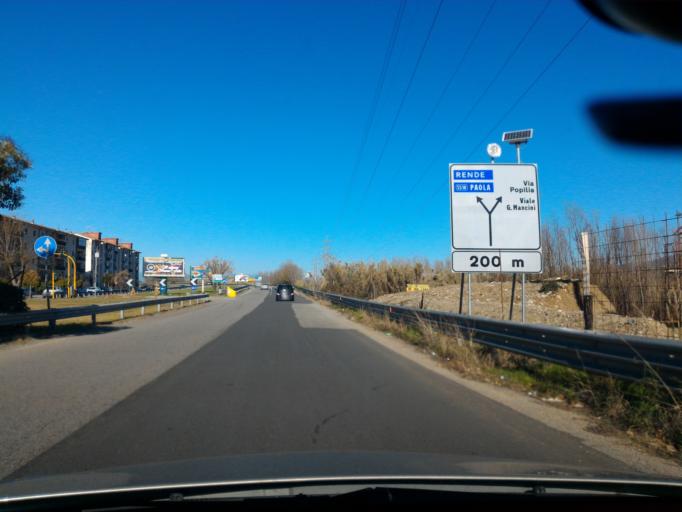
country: IT
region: Calabria
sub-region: Provincia di Cosenza
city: Cosenza
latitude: 39.3246
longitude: 16.2560
